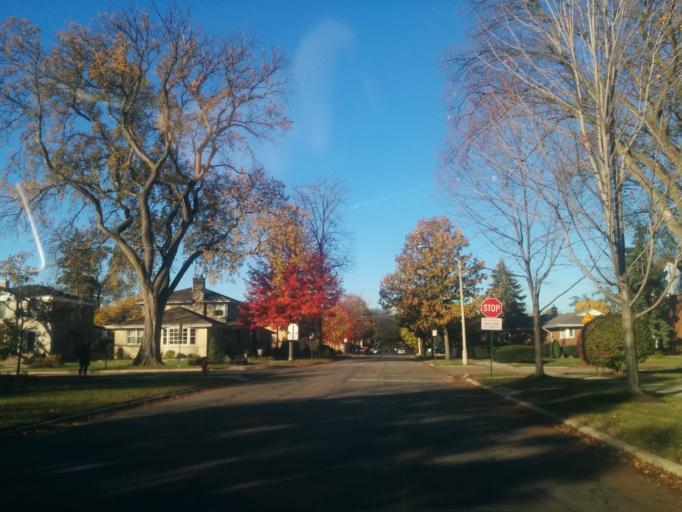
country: US
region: Illinois
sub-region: Cook County
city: River Forest
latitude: 41.9070
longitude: -87.8037
